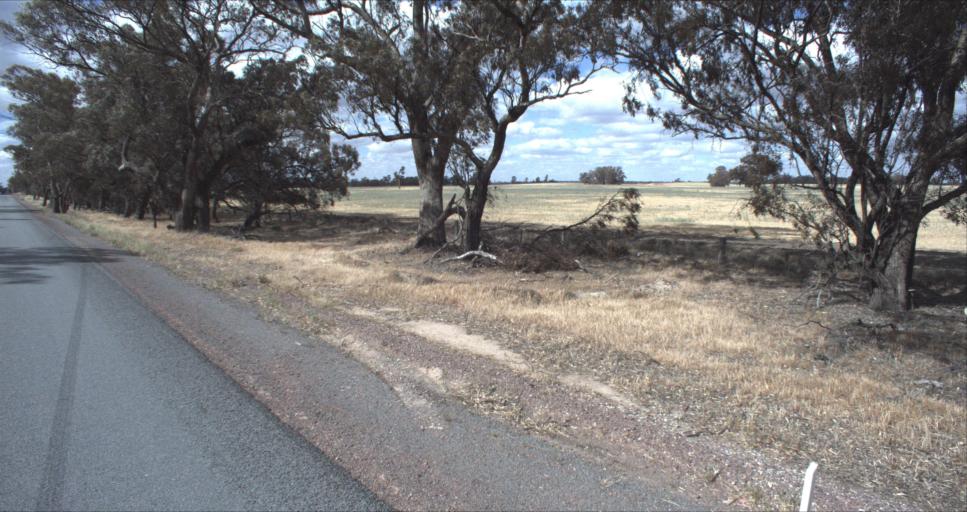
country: AU
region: New South Wales
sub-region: Leeton
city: Leeton
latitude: -34.6780
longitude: 146.3461
